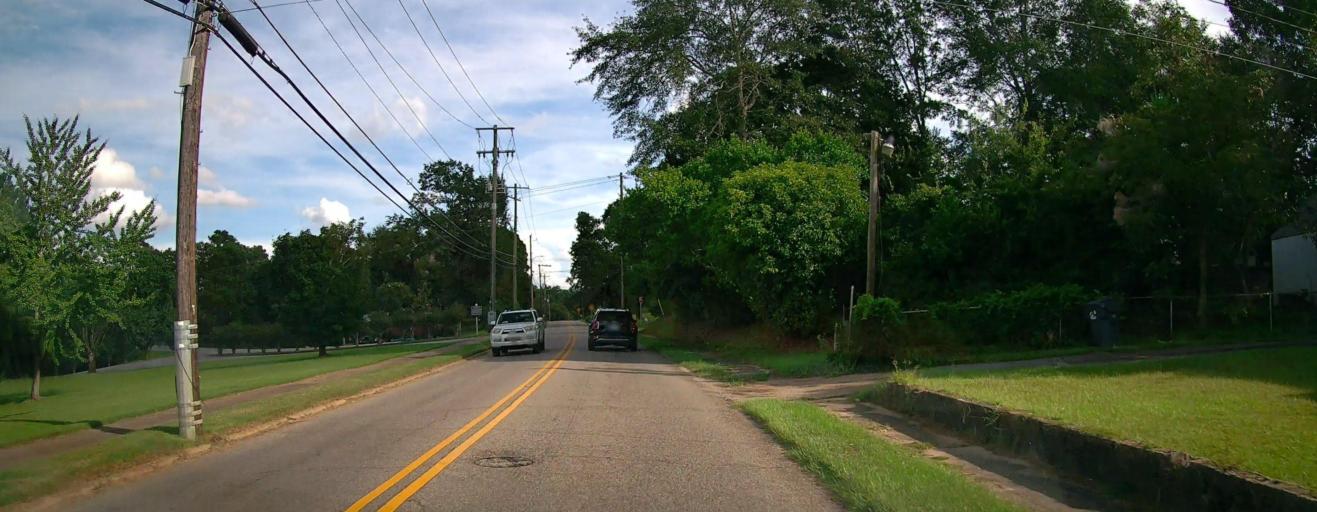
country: US
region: Alabama
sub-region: Russell County
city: Phenix City
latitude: 32.4866
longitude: -85.0084
